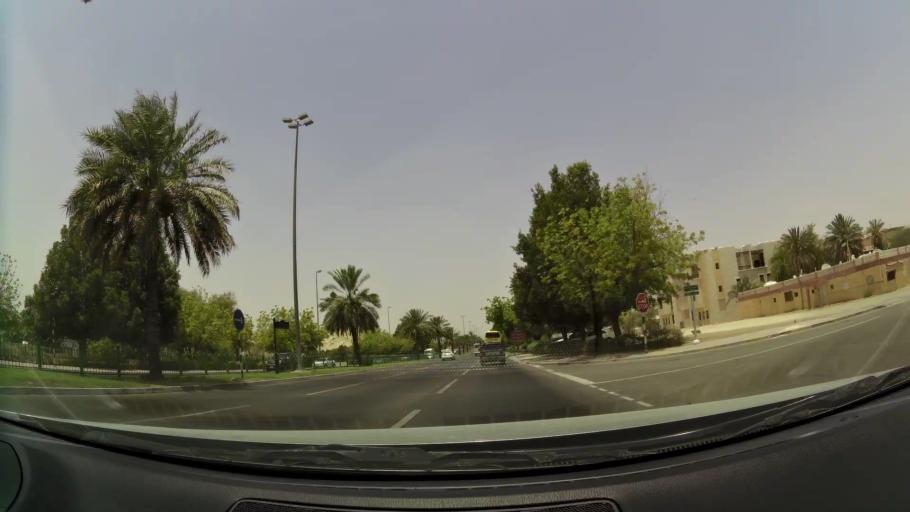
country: AE
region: Abu Dhabi
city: Al Ain
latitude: 24.2059
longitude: 55.7734
